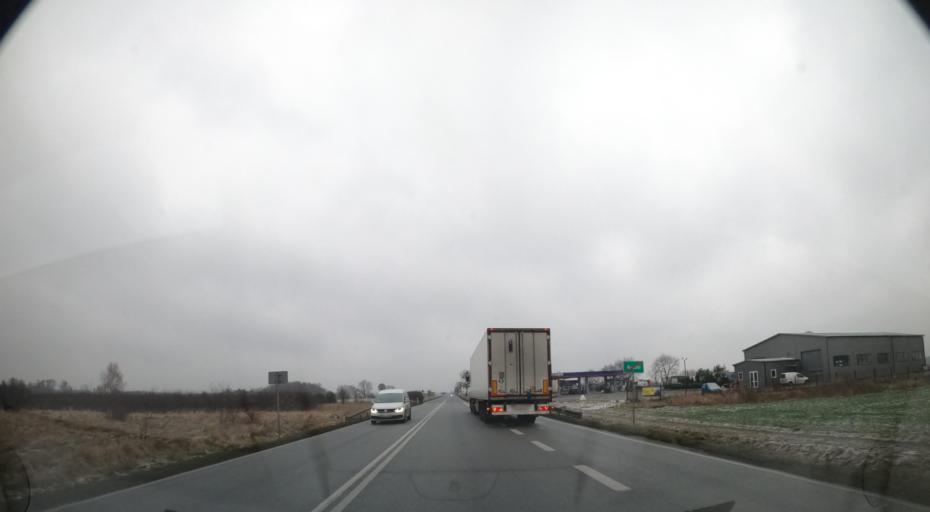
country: PL
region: Masovian Voivodeship
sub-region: Powiat sochaczewski
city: Mlodzieszyn
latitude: 52.2709
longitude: 20.1660
